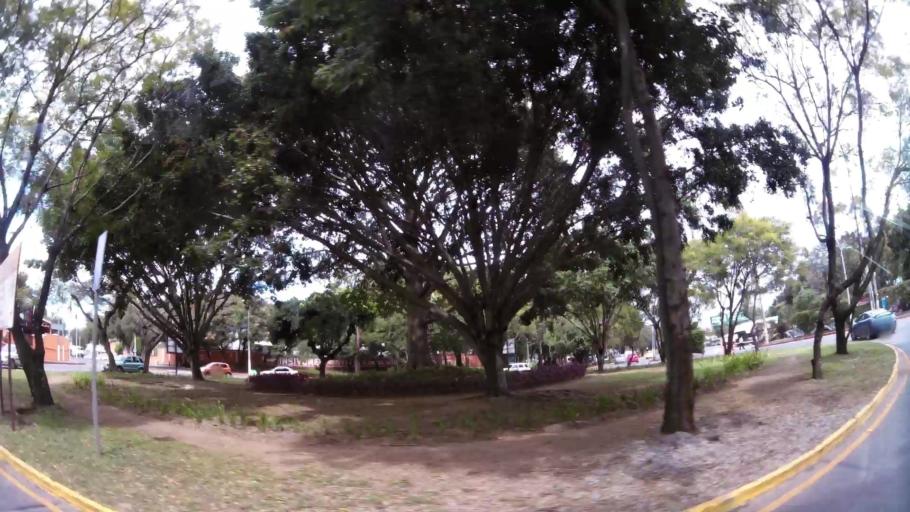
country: GT
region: Guatemala
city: Santa Catarina Pinula
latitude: 14.5865
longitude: -90.5320
